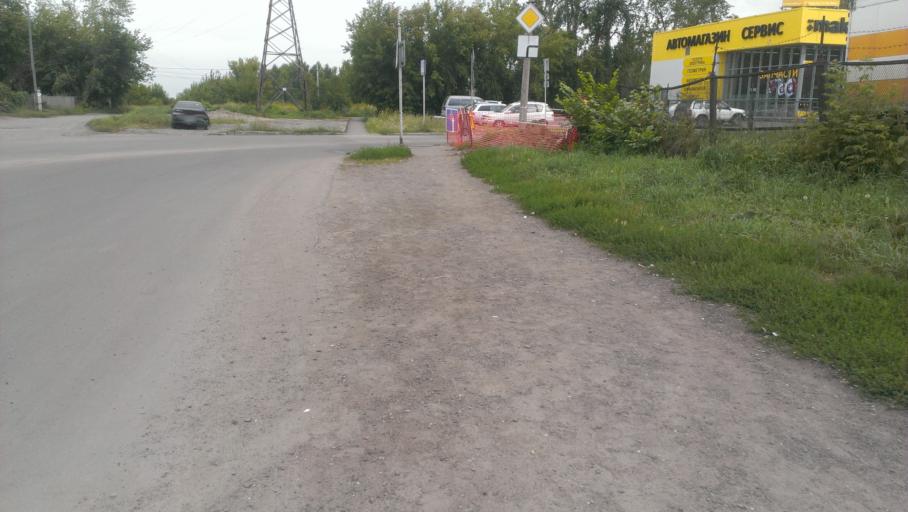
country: RU
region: Altai Krai
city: Yuzhnyy
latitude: 53.2553
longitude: 83.7021
